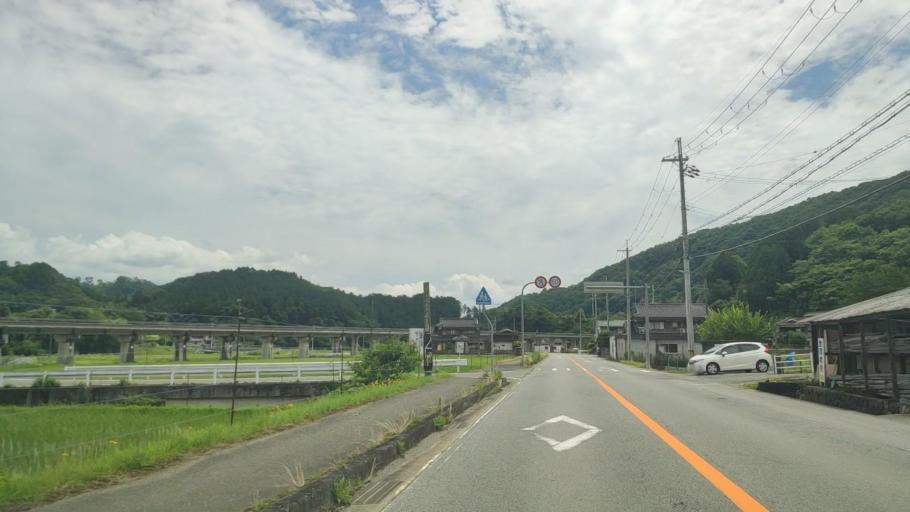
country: JP
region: Hyogo
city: Yamazakicho-nakabirose
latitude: 35.0371
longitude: 134.3678
